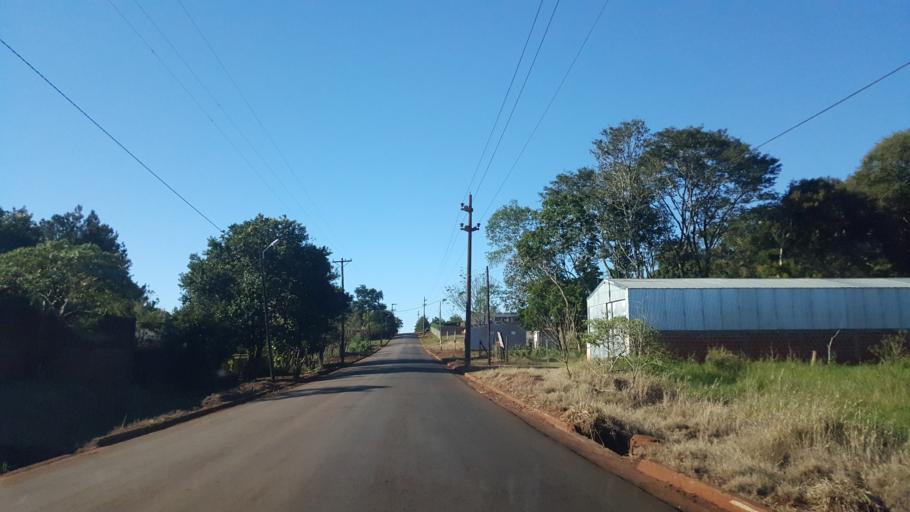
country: AR
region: Misiones
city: Gobernador Roca
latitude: -27.1837
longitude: -55.4602
